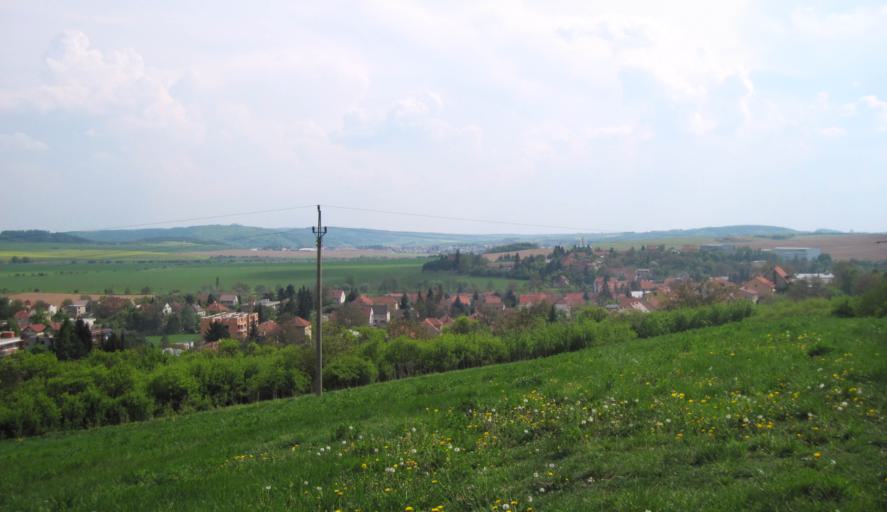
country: CZ
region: South Moravian
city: Ricany
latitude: 49.2193
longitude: 16.3995
